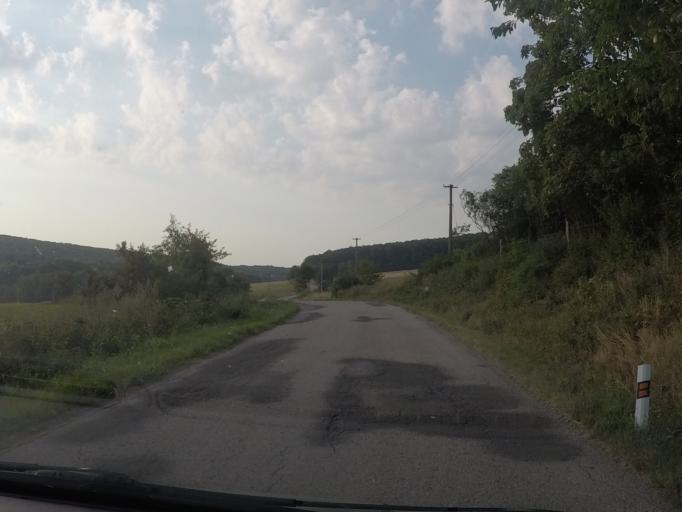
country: SK
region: Nitriansky
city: Zlate Moravce
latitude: 48.4550
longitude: 18.3209
